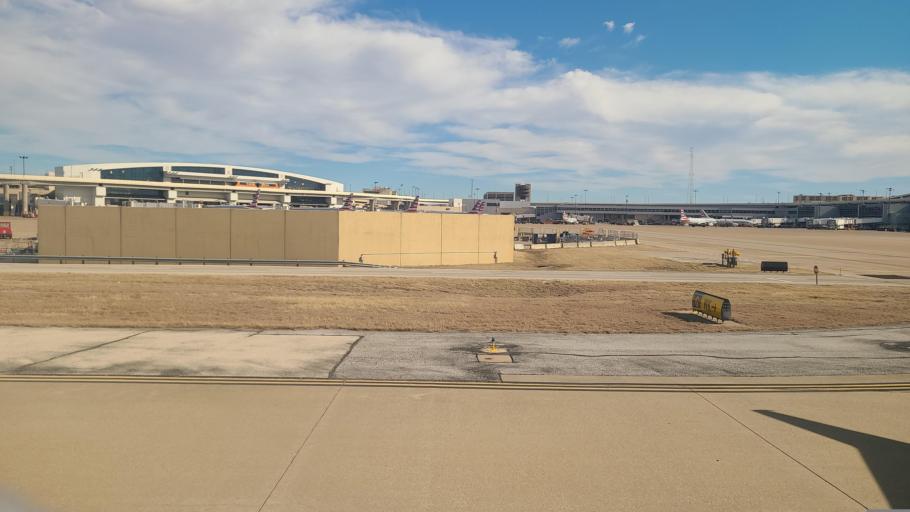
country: US
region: Texas
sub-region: Tarrant County
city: Grapevine
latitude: 32.9018
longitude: -97.0476
